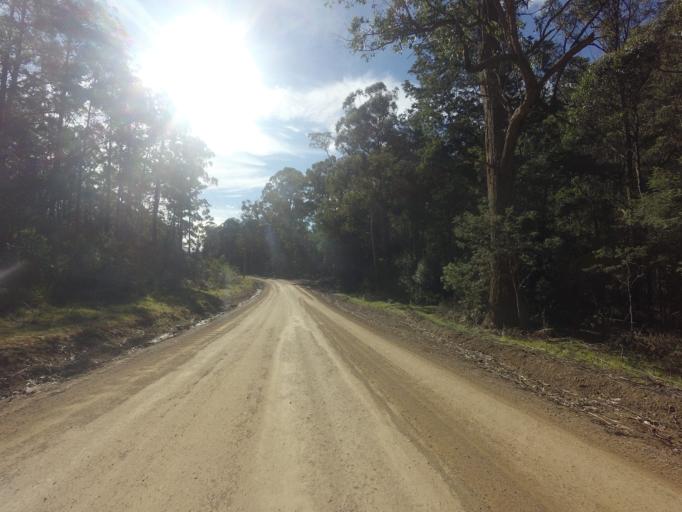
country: AU
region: Tasmania
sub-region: Clarence
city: Sandford
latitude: -43.1255
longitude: 147.7634
